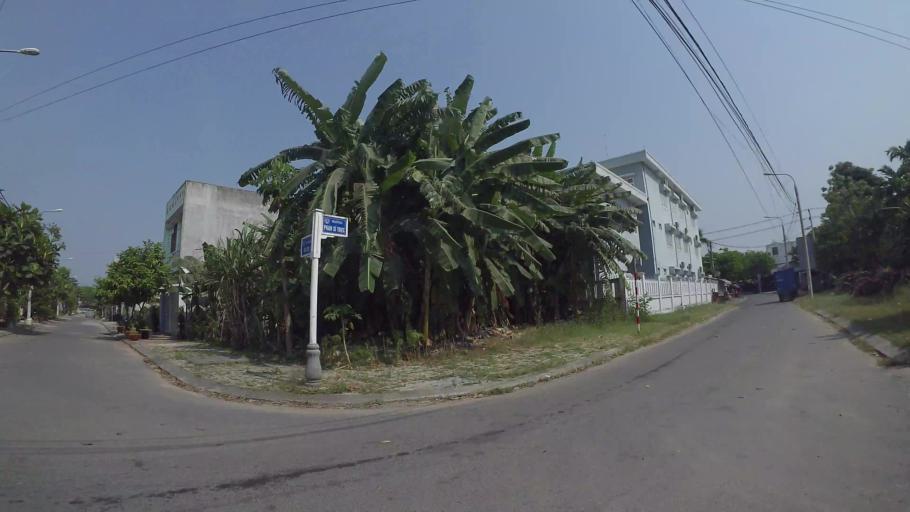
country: VN
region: Da Nang
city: Cam Le
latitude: 16.0121
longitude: 108.1970
